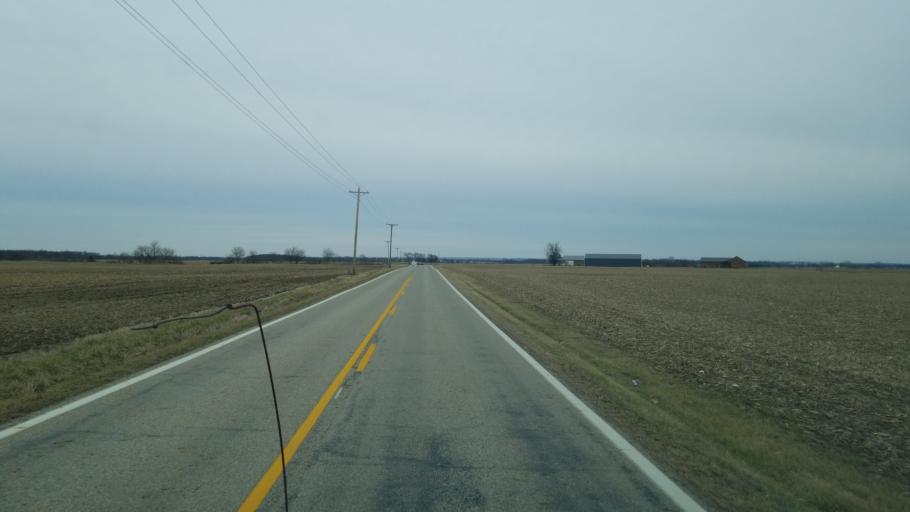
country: US
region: Ohio
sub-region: Pickaway County
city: Williamsport
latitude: 39.5555
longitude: -83.0996
